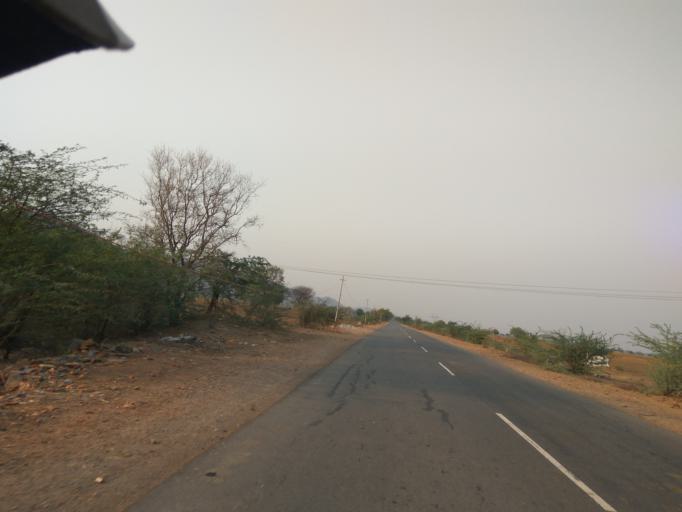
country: IN
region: Andhra Pradesh
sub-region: Prakasam
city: Cumbum
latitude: 15.6432
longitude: 79.1436
